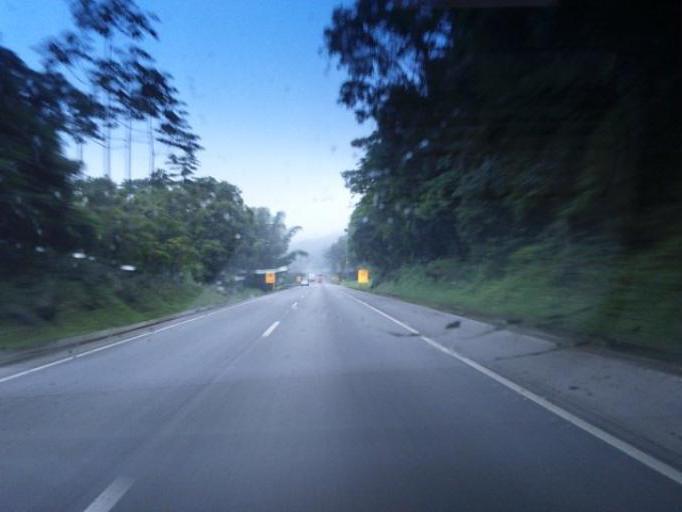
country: BR
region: Parana
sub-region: Guaratuba
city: Guaratuba
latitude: -25.9121
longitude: -48.9201
